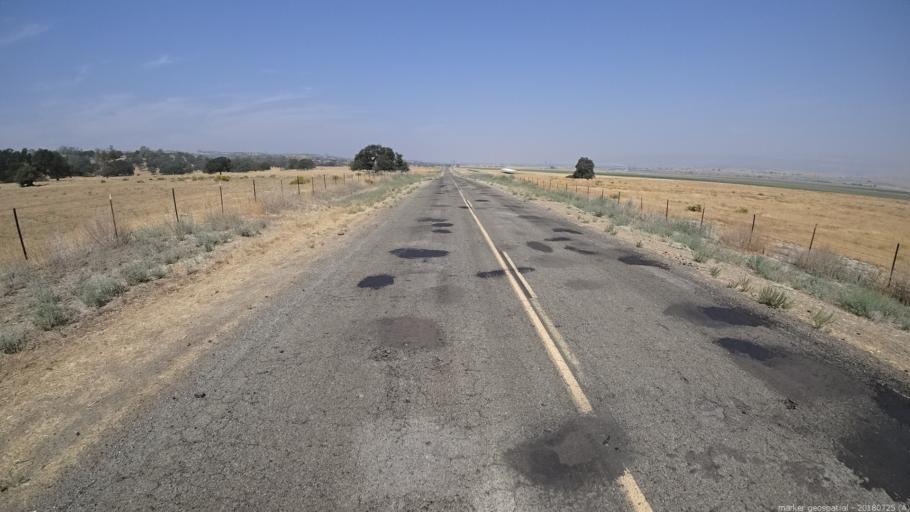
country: US
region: California
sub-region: San Luis Obispo County
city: Shandon
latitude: 35.8092
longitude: -120.3712
